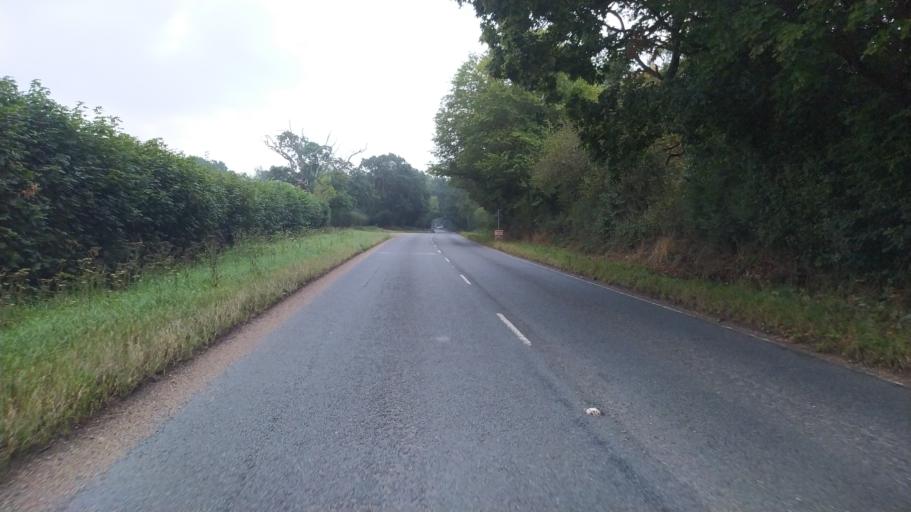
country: GB
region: England
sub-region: Hampshire
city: New Milton
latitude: 50.7684
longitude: -1.6973
